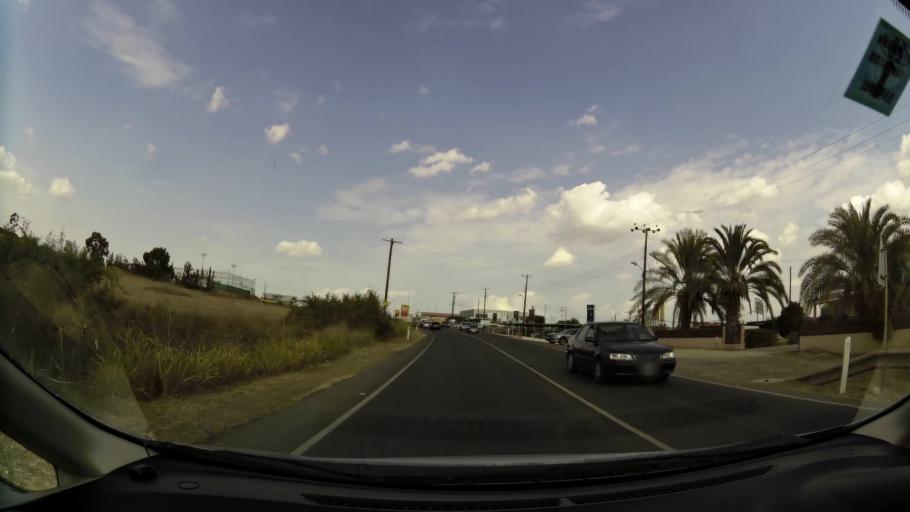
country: CY
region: Lefkosia
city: Tseri
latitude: 35.0952
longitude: 33.3271
